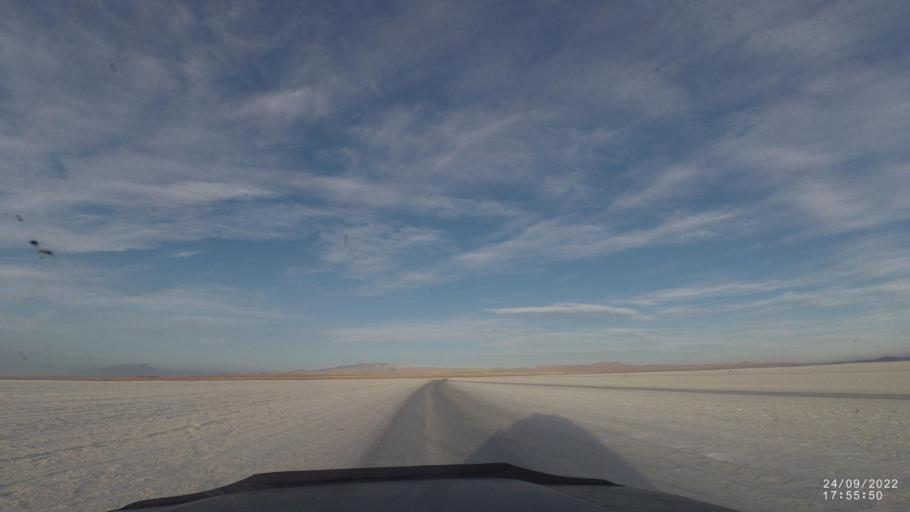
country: BO
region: Potosi
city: Colchani
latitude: -20.3262
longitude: -67.0241
